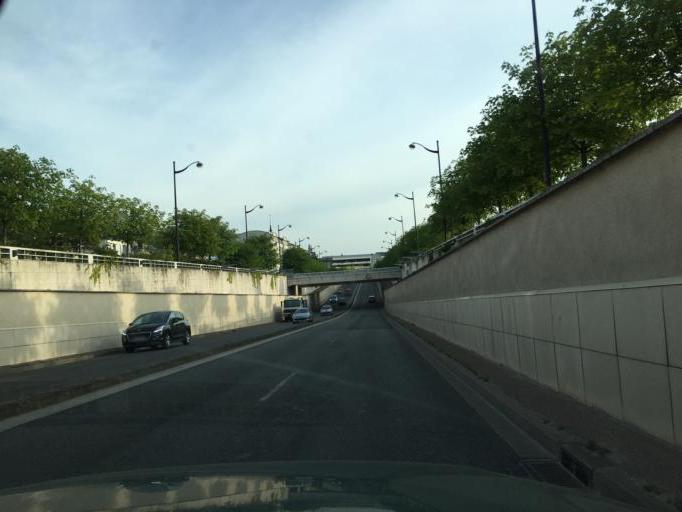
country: FR
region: Centre
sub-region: Departement du Loiret
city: Saint-Jean-le-Blanc
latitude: 47.9089
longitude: 1.9226
